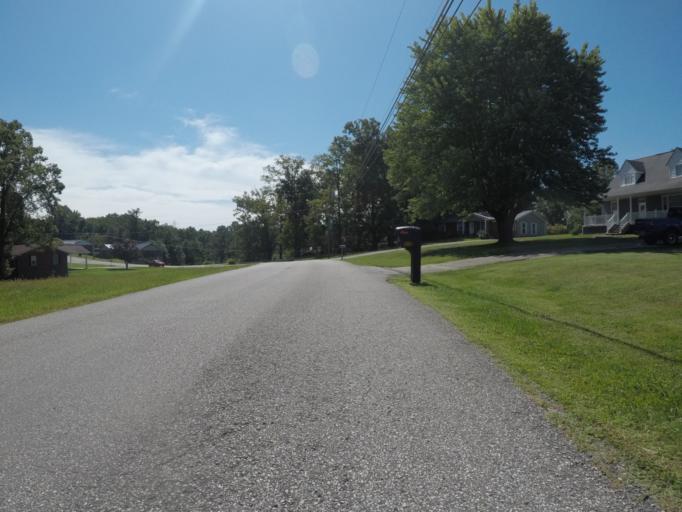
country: US
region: Kentucky
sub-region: Boyd County
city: Meads
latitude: 38.4121
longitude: -82.6581
